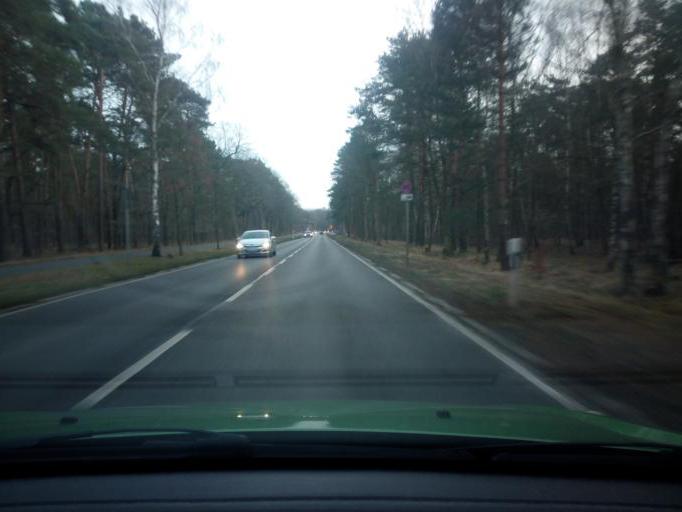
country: DE
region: Berlin
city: Friedrichshagen
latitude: 52.4323
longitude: 13.6097
